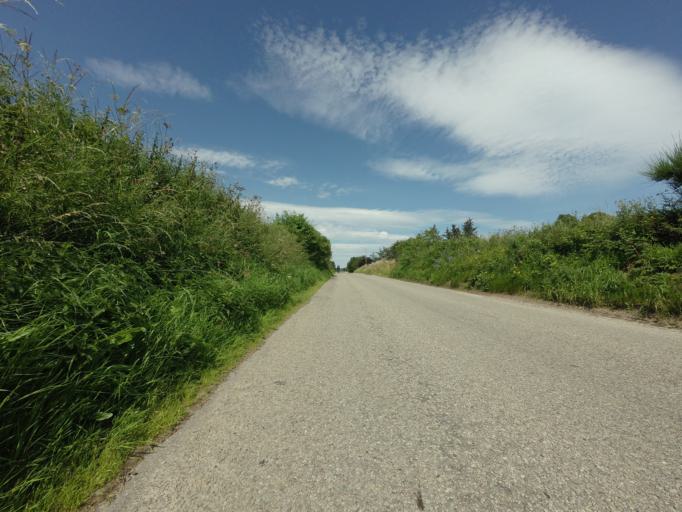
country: GB
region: Scotland
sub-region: Highland
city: Inverness
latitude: 57.5256
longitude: -4.3165
